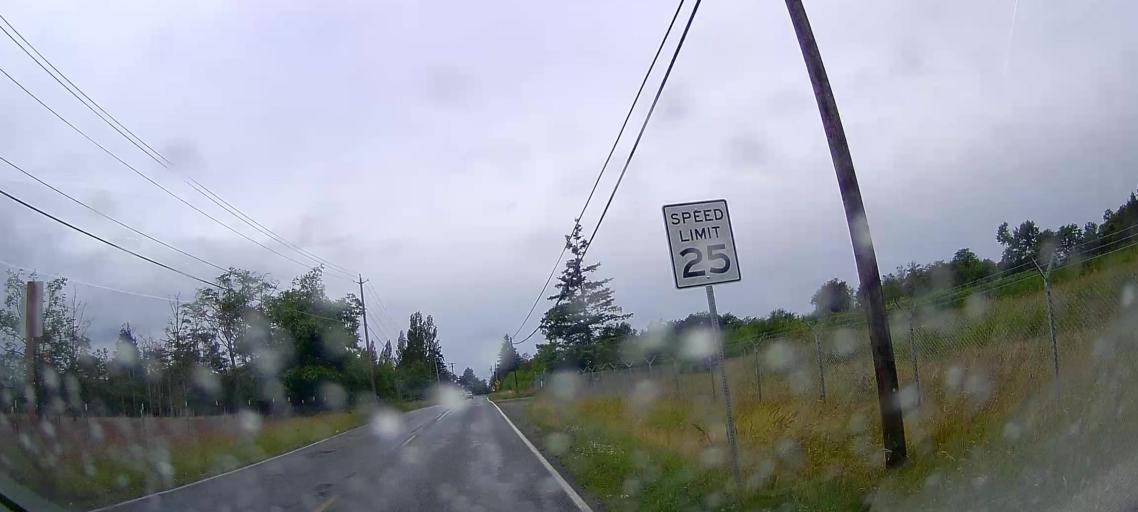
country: US
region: Washington
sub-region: Whatcom County
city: Birch Bay
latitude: 48.8196
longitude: -122.7040
